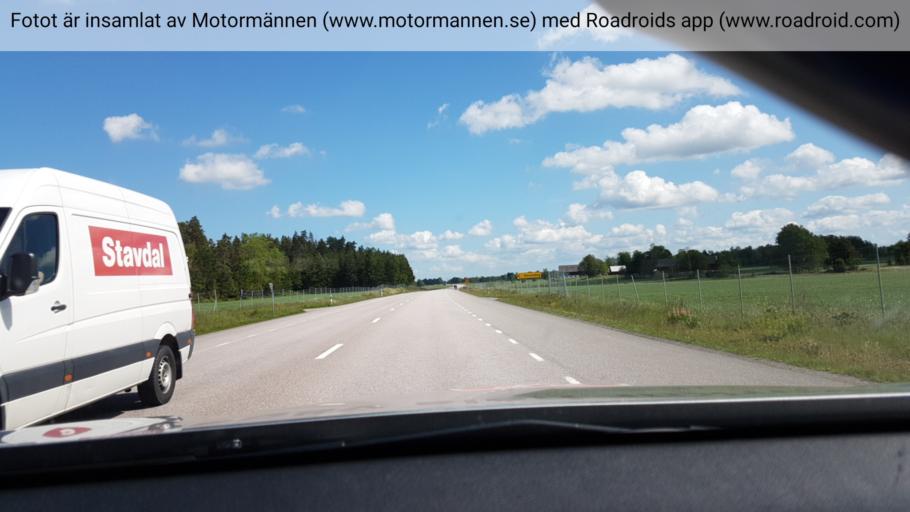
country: SE
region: Vaestra Goetaland
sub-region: Grastorps Kommun
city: Graestorp
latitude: 58.3066
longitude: 12.5475
